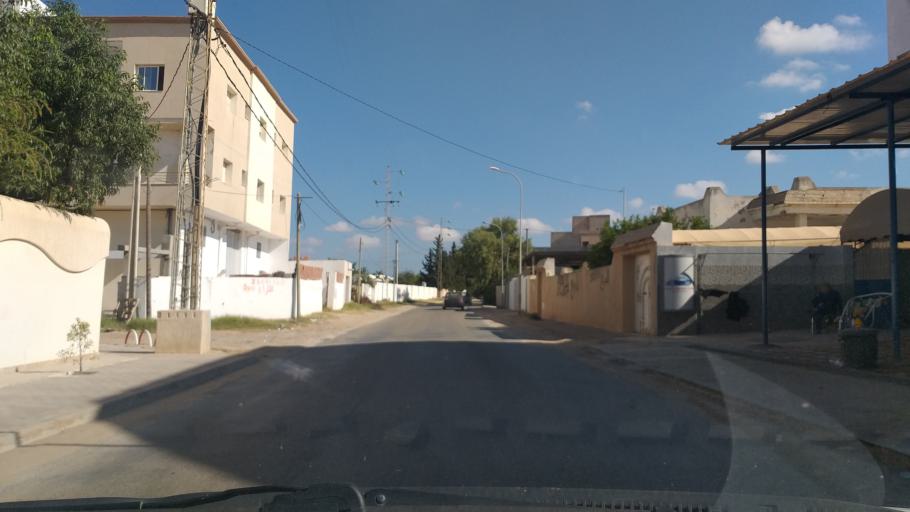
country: TN
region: Safaqis
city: Al Qarmadah
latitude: 34.8024
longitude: 10.7773
